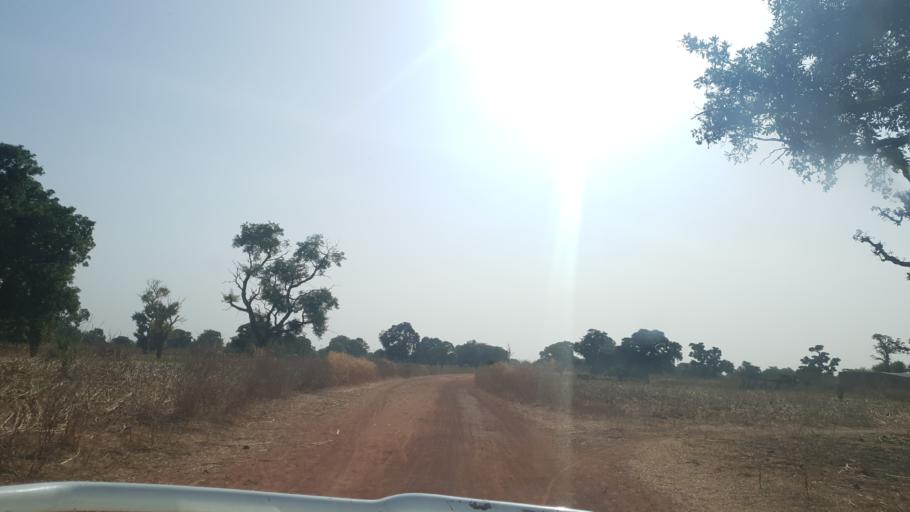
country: ML
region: Koulikoro
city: Dioila
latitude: 12.7062
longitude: -6.7711
